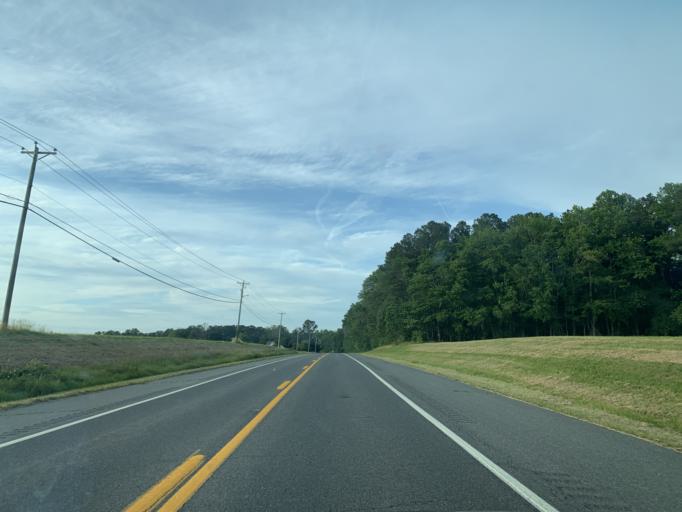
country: US
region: Virginia
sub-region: Accomack County
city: Captains Cove
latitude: 38.0782
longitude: -75.4012
